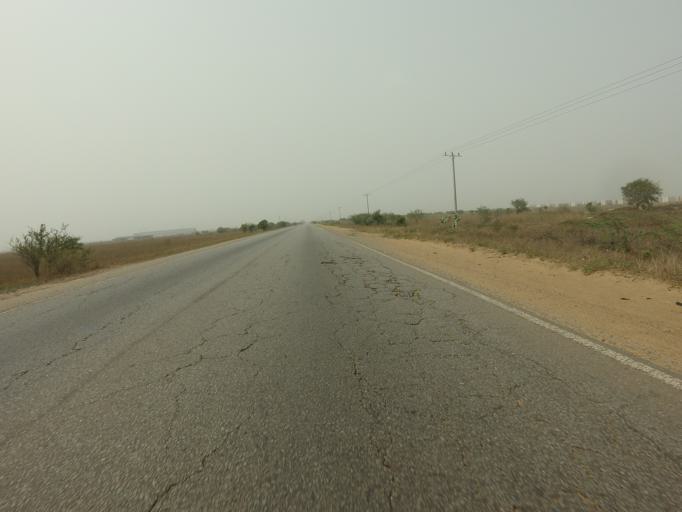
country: GH
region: Greater Accra
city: Tema
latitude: 5.8305
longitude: 0.2074
